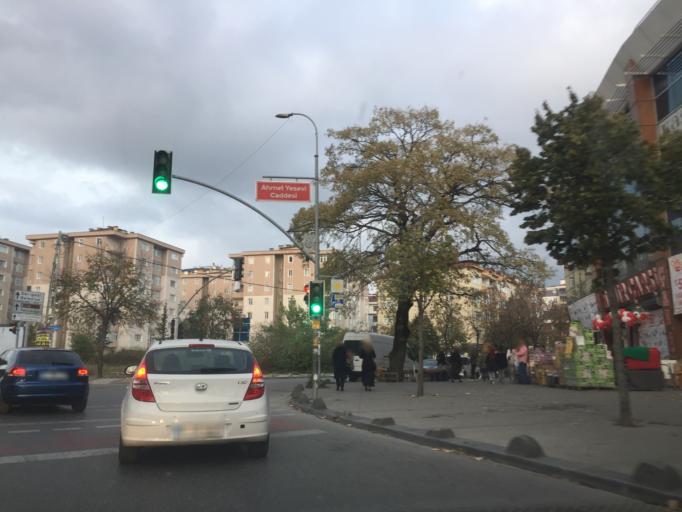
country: TR
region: Istanbul
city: Samandira
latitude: 40.9854
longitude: 29.2327
